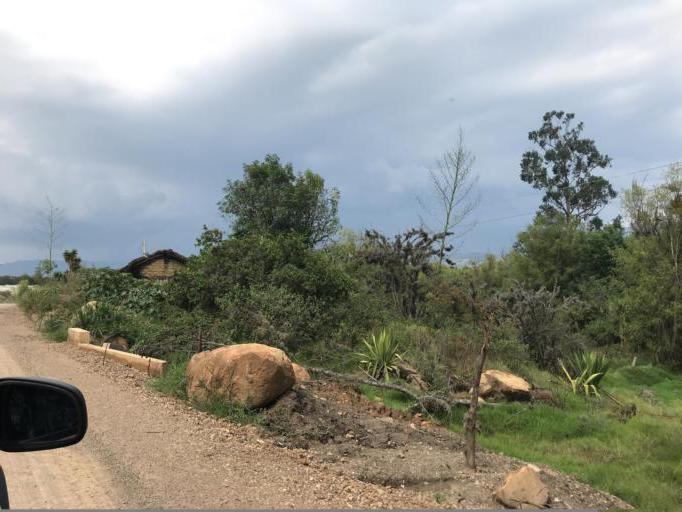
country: CO
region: Boyaca
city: Villa de Leiva
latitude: 5.6490
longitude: -73.5917
